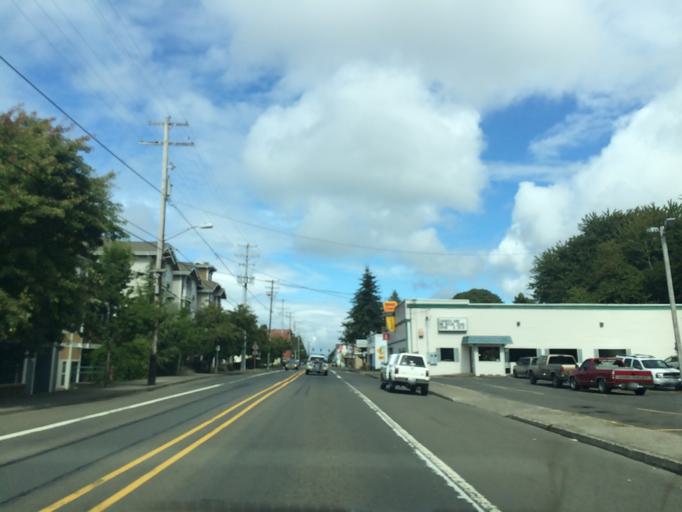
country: US
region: Oregon
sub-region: Clatsop County
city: Astoria
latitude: 46.1891
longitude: -123.8136
